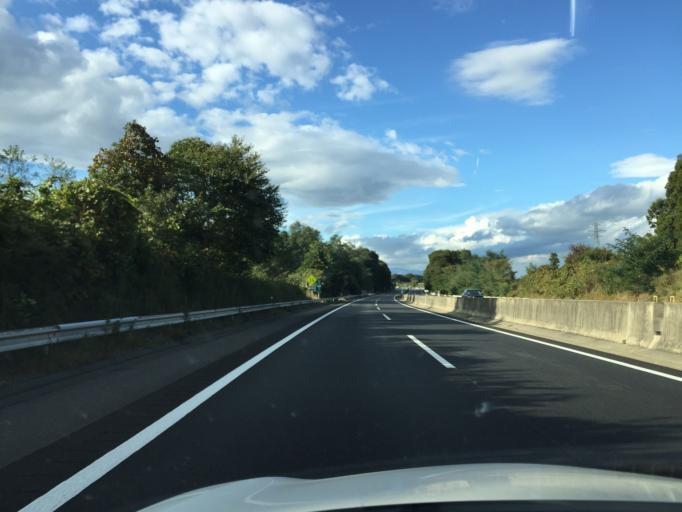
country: JP
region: Fukushima
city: Sukagawa
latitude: 37.3117
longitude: 140.3440
